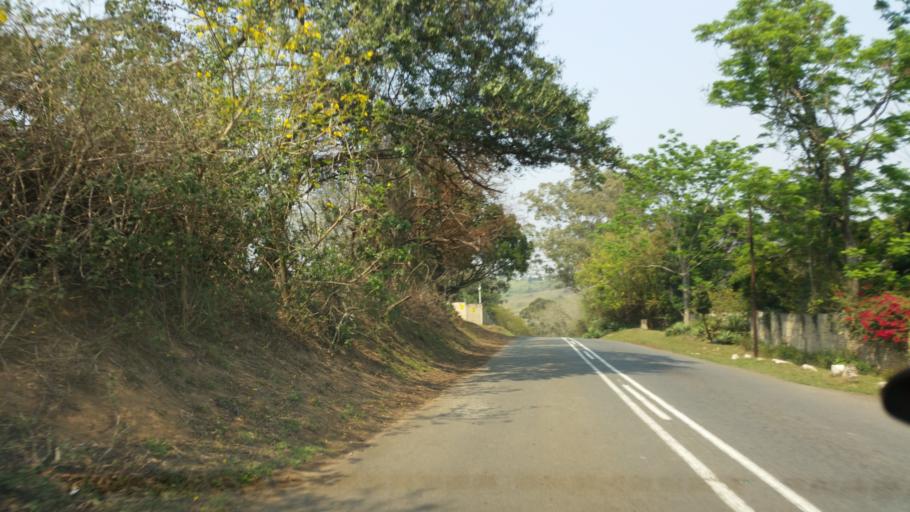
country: ZA
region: KwaZulu-Natal
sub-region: eThekwini Metropolitan Municipality
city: Mpumalanga
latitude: -29.7364
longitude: 30.6641
